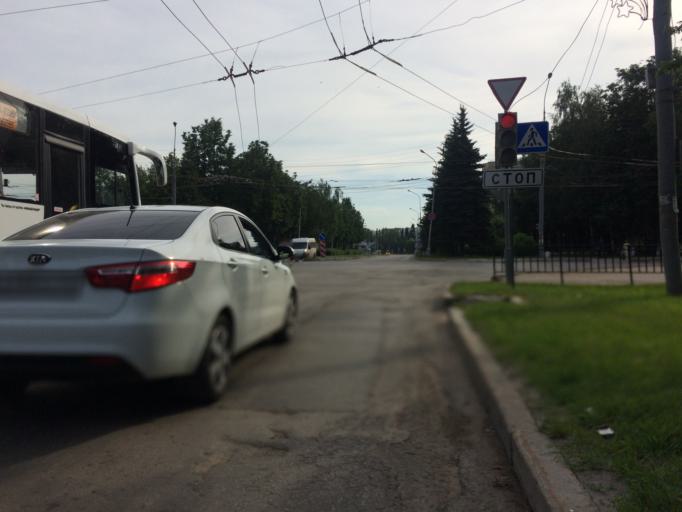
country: RU
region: Mariy-El
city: Yoshkar-Ola
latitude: 56.6232
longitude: 47.8841
